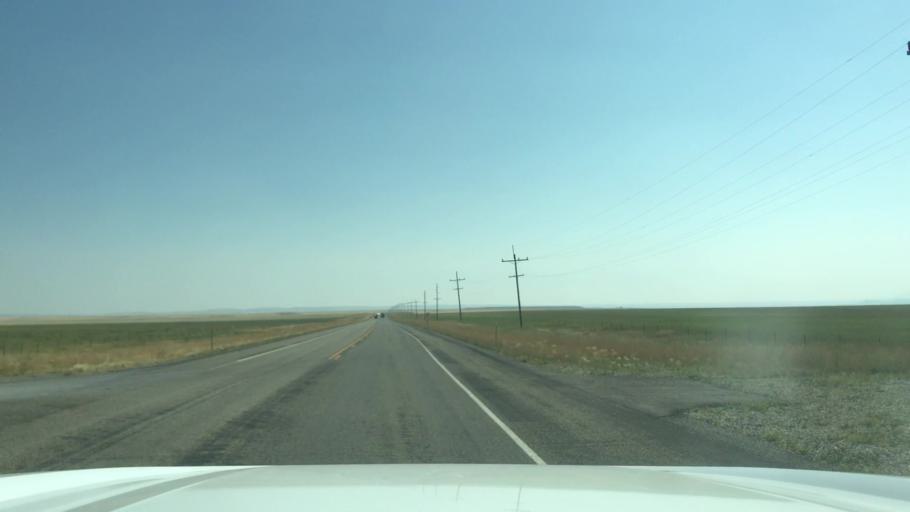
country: US
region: Montana
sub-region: Wheatland County
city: Harlowton
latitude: 46.5192
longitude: -109.7660
